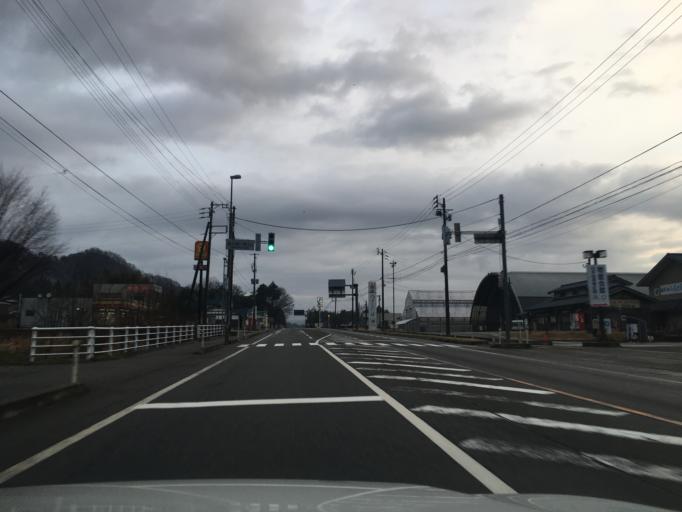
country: JP
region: Niigata
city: Murakami
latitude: 38.2828
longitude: 139.5220
